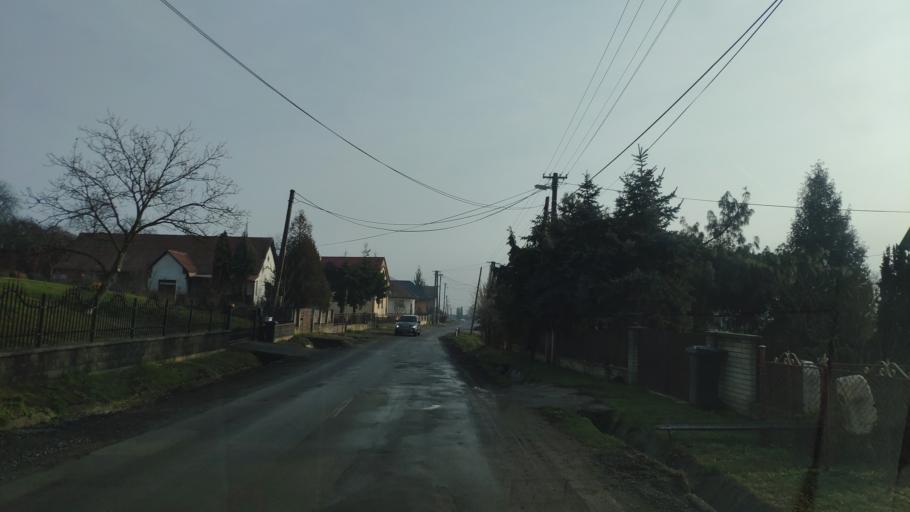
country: SK
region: Kosicky
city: Kosice
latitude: 48.7063
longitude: 21.4068
